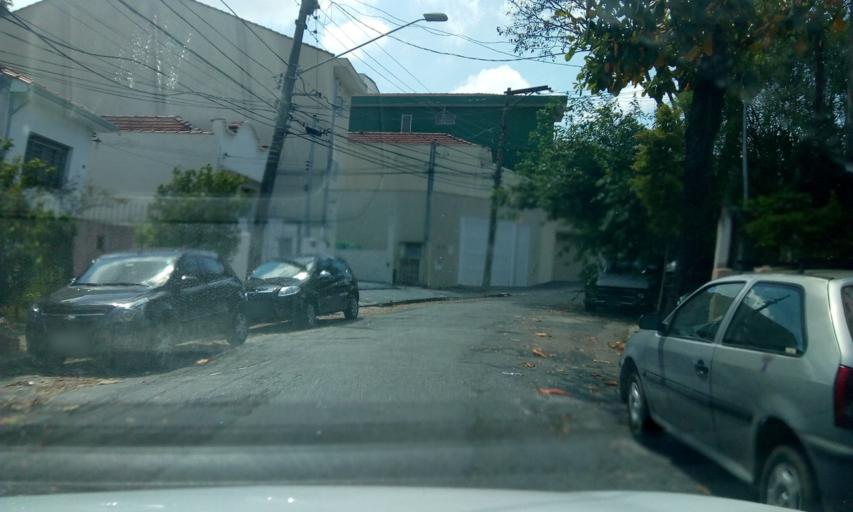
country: BR
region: Sao Paulo
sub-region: Sao Paulo
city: Sao Paulo
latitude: -23.5333
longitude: -46.7073
